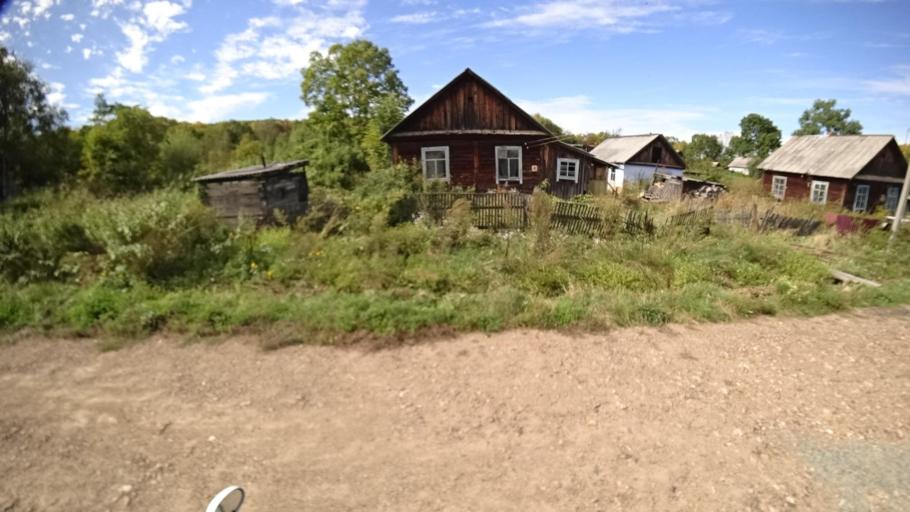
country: RU
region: Primorskiy
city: Yakovlevka
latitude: 44.3970
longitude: 133.6002
